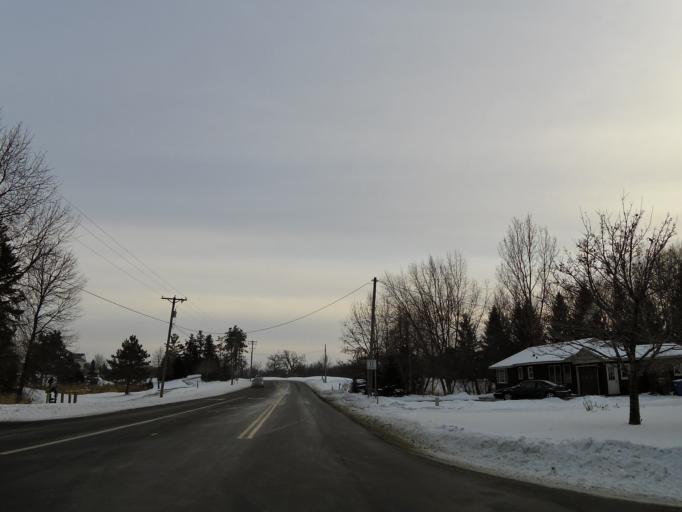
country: US
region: Minnesota
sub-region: Carver County
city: Victoria
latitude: 44.8524
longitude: -93.6599
